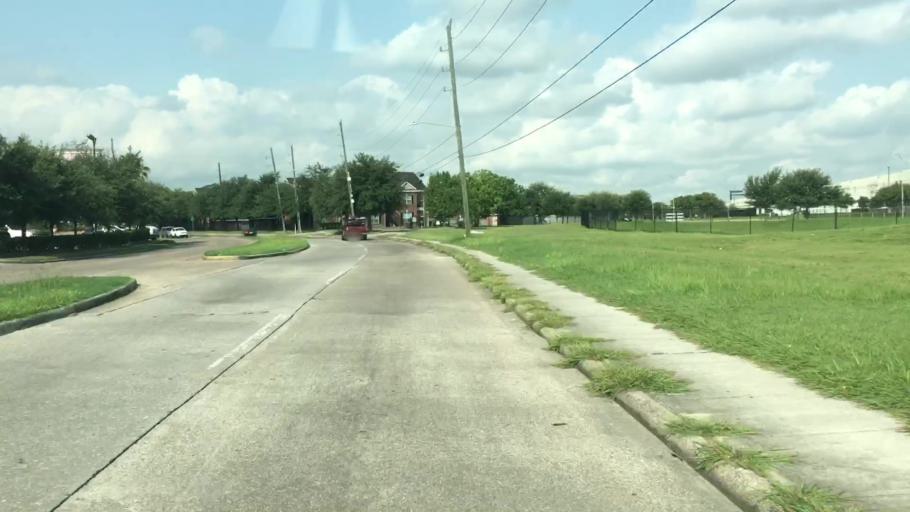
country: US
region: Texas
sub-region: Harris County
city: Aldine
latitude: 29.9349
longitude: -95.3997
